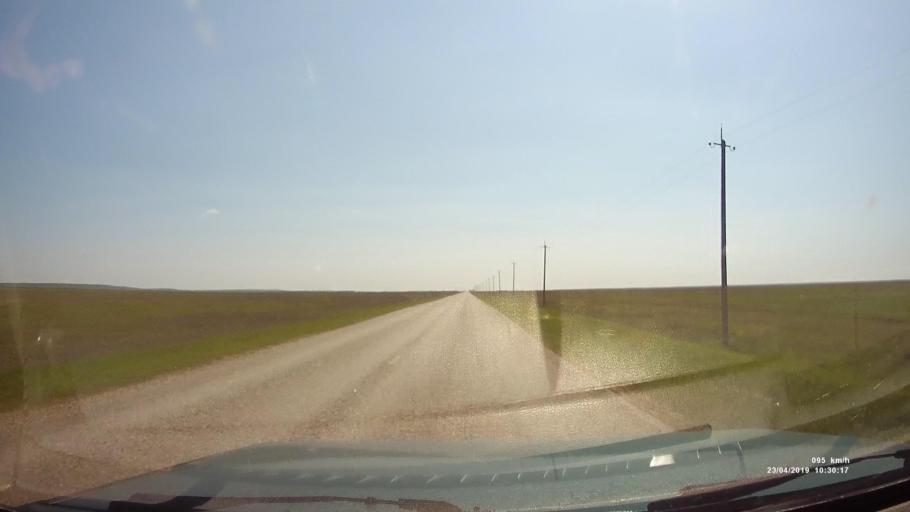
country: RU
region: Kalmykiya
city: Yashalta
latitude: 46.5930
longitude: 42.5418
